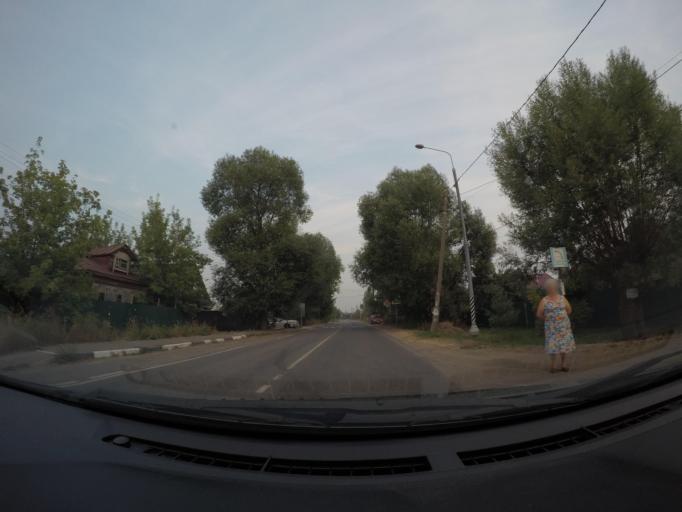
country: RU
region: Moskovskaya
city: Imeni Tsyurupy
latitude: 55.4936
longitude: 38.6638
